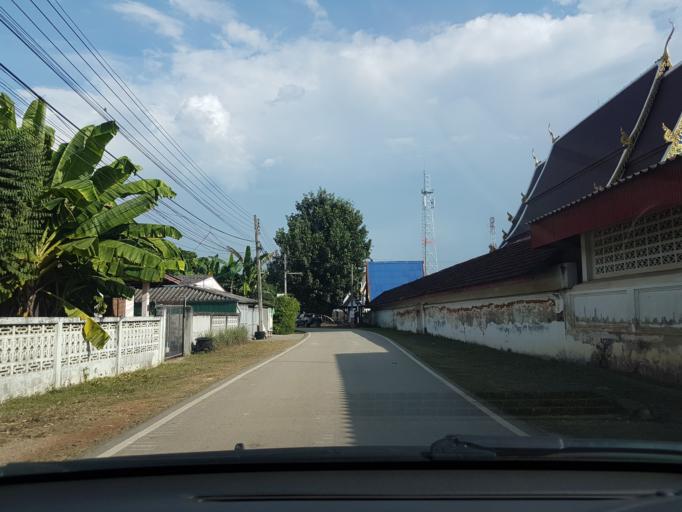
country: TH
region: Lampang
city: Ko Kha
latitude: 18.2179
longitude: 99.4190
